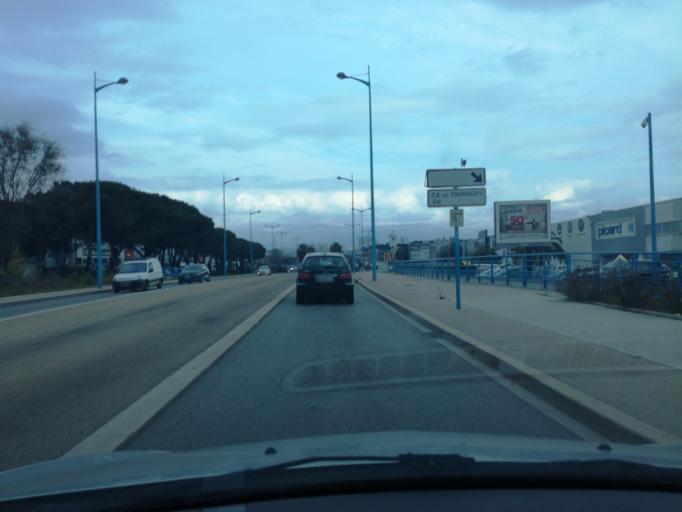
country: FR
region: Provence-Alpes-Cote d'Azur
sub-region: Departement des Alpes-Maritimes
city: Mandelieu-la-Napoule
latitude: 43.5531
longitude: 6.9551
